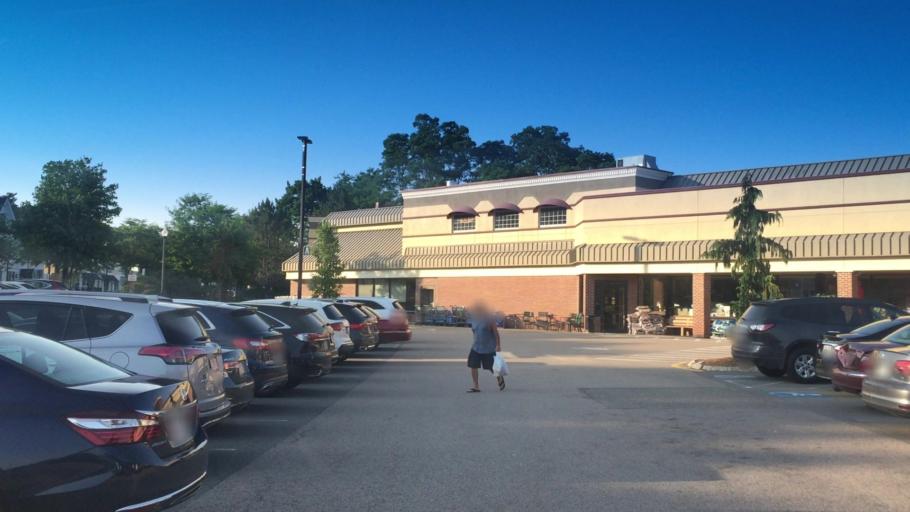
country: US
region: Massachusetts
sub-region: Norfolk County
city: Norwood
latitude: 42.2171
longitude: -71.1884
